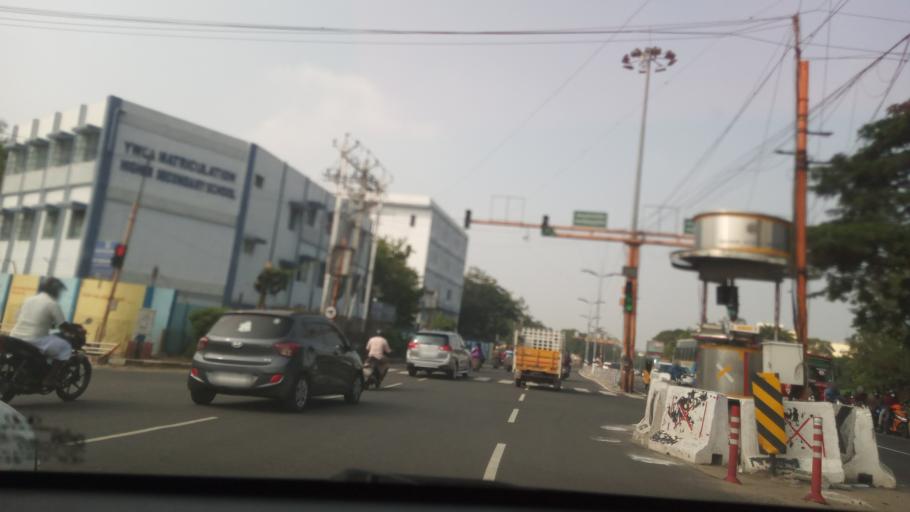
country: IN
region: Tamil Nadu
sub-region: Coimbatore
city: Coimbatore
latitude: 11.0039
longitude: 76.9725
